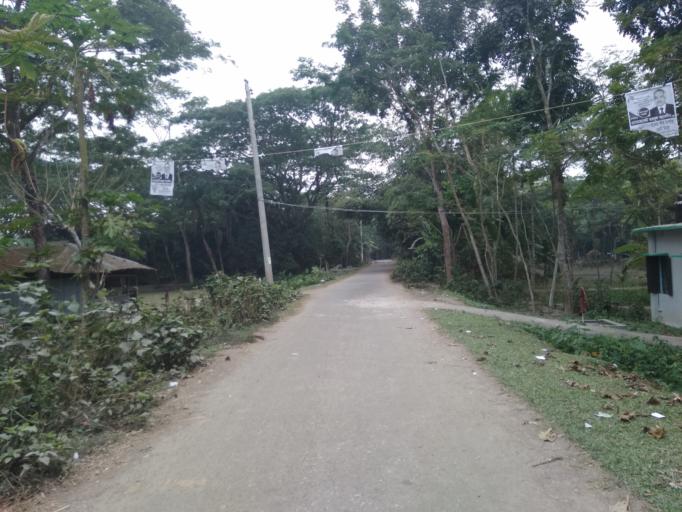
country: BD
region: Barisal
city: Mehendiganj
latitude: 22.9212
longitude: 90.3916
